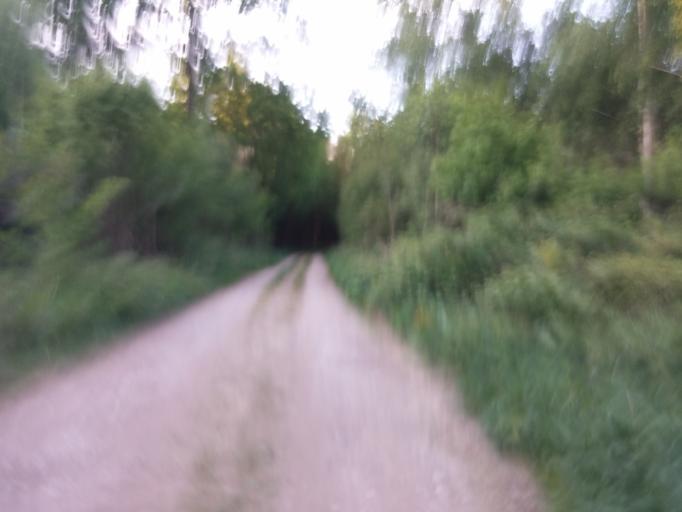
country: DE
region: Bavaria
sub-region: Upper Bavaria
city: Zorneding
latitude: 48.1144
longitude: 11.8166
